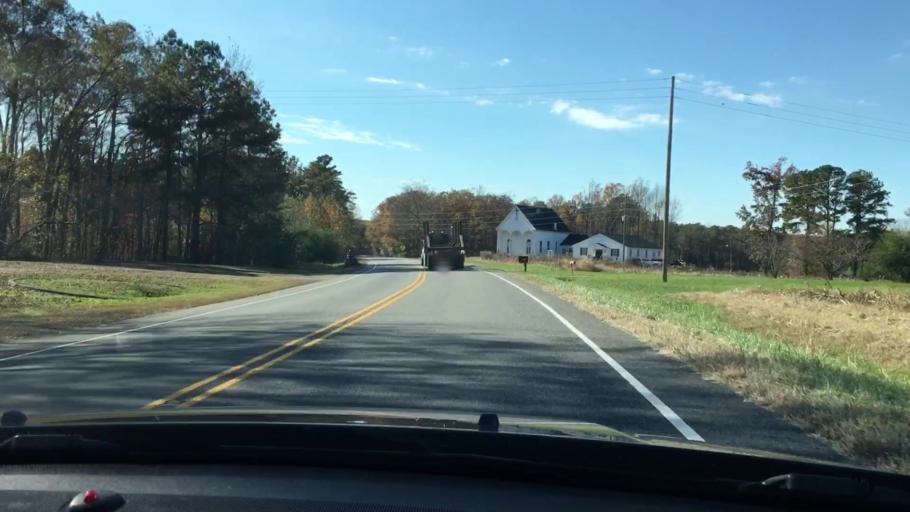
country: US
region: Virginia
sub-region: King William County
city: Central Garage
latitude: 37.7916
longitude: -77.2105
